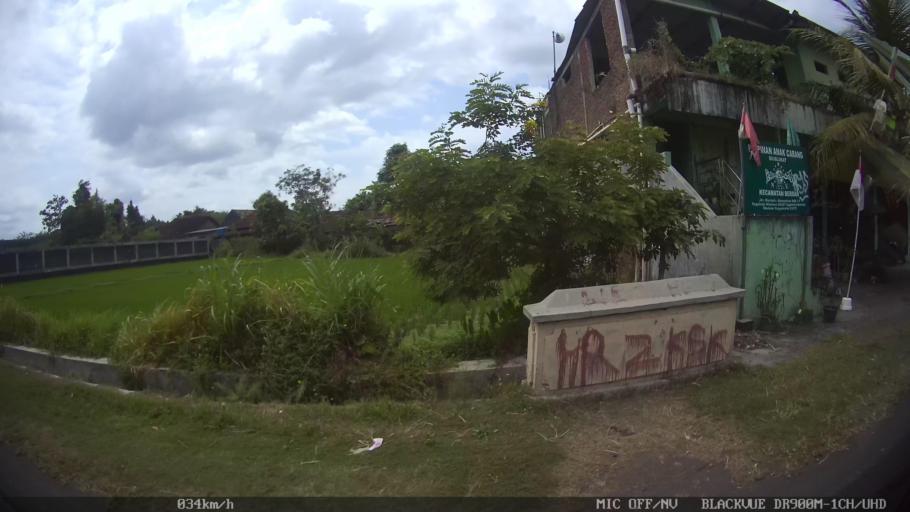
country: ID
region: Daerah Istimewa Yogyakarta
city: Depok
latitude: -7.8165
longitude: 110.4430
